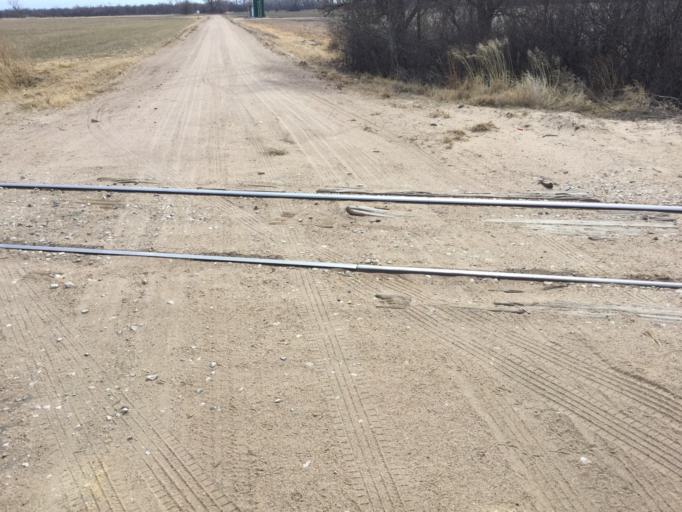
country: US
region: Kansas
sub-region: Barton County
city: Ellinwood
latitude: 38.2738
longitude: -98.4067
